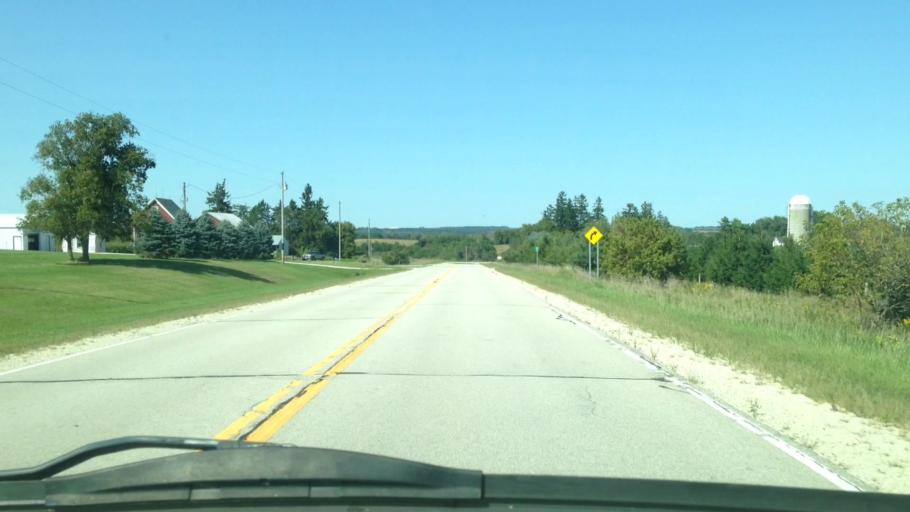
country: US
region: Minnesota
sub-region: Houston County
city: Spring Grove
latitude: 43.6383
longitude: -91.7903
